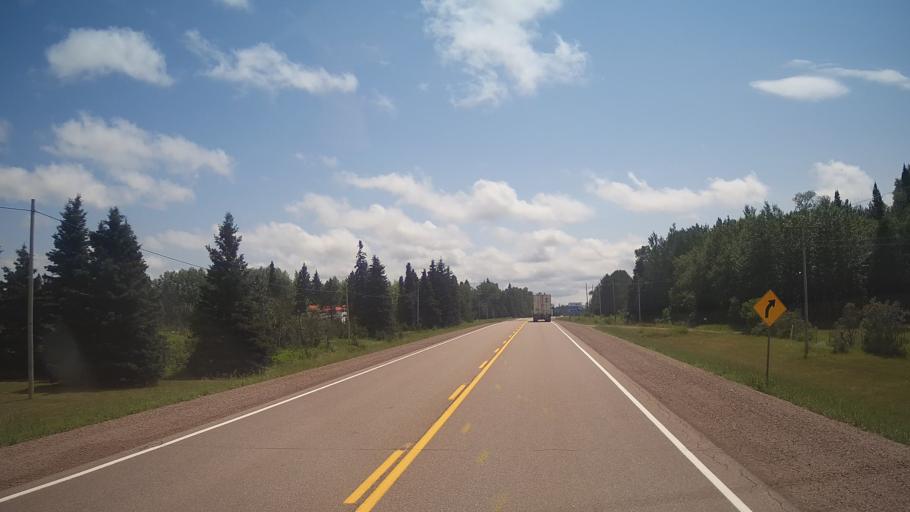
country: CA
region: Ontario
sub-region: Thunder Bay District
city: Thunder Bay
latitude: 48.8296
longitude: -88.5276
